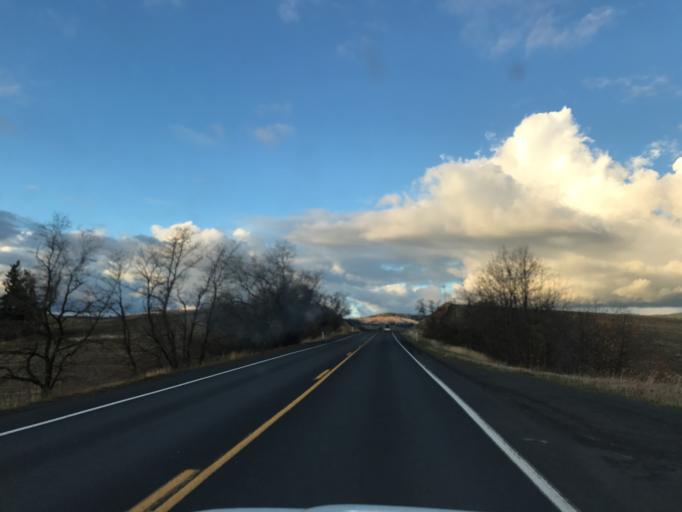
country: US
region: Idaho
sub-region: Latah County
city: Moscow
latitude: 46.7619
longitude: -117.0017
